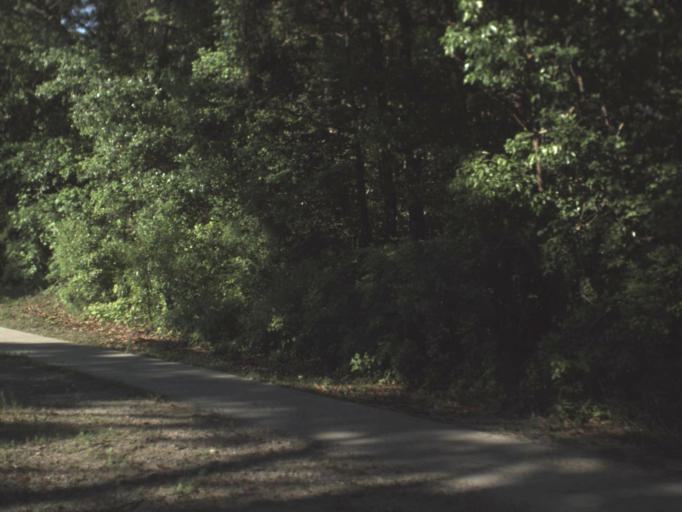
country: US
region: Florida
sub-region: Gulf County
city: Wewahitchka
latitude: 30.0221
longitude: -84.9798
